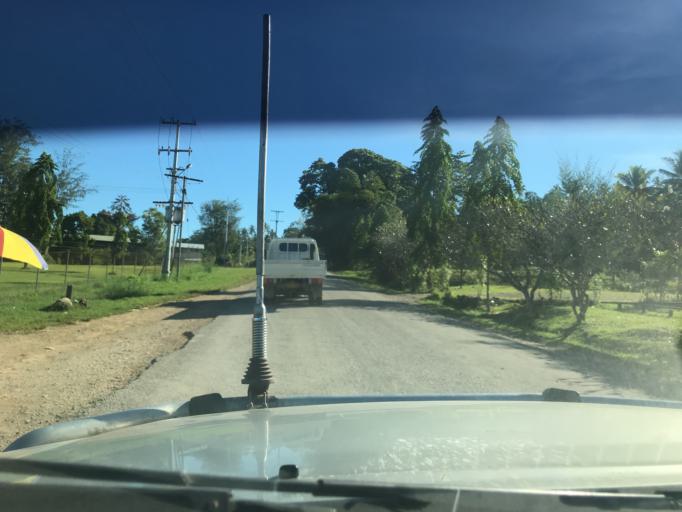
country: SB
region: Malaita
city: Auki
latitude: -8.7632
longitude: 160.6957
